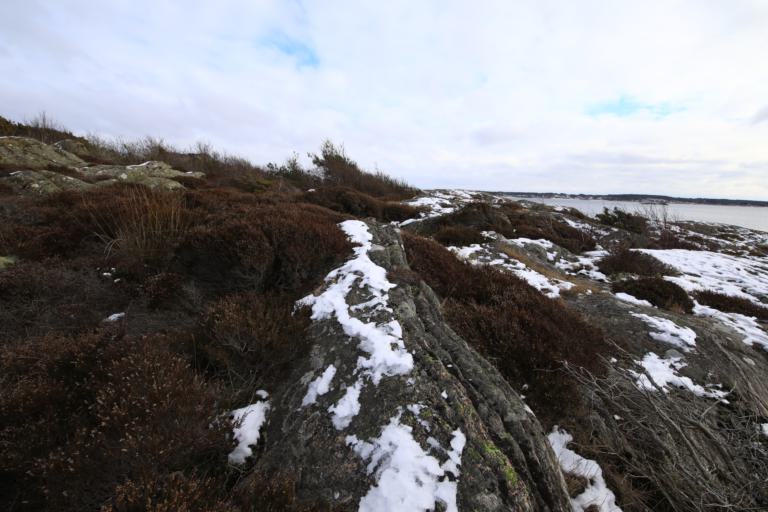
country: SE
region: Halland
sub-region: Kungsbacka Kommun
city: Frillesas
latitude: 57.2147
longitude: 12.1569
